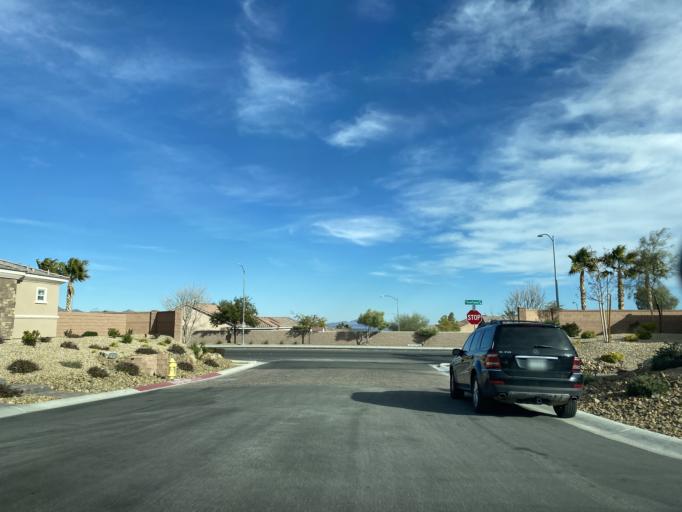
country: US
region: Nevada
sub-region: Clark County
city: Summerlin South
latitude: 36.2914
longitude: -115.3065
